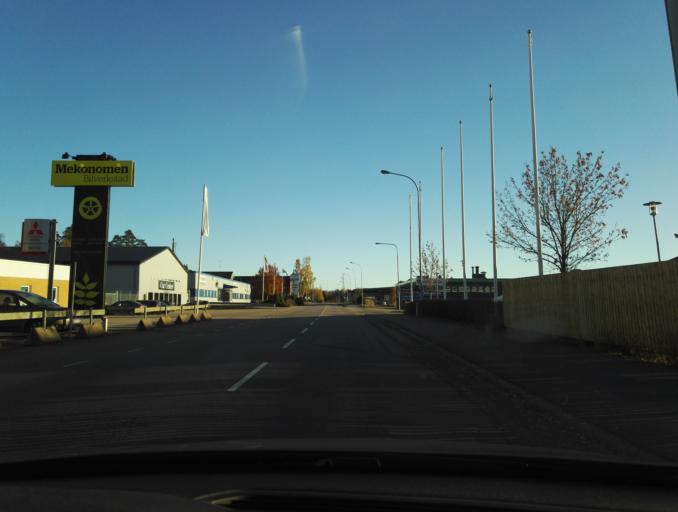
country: SE
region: Kronoberg
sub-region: Vaxjo Kommun
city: Vaexjoe
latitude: 56.8918
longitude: 14.7711
